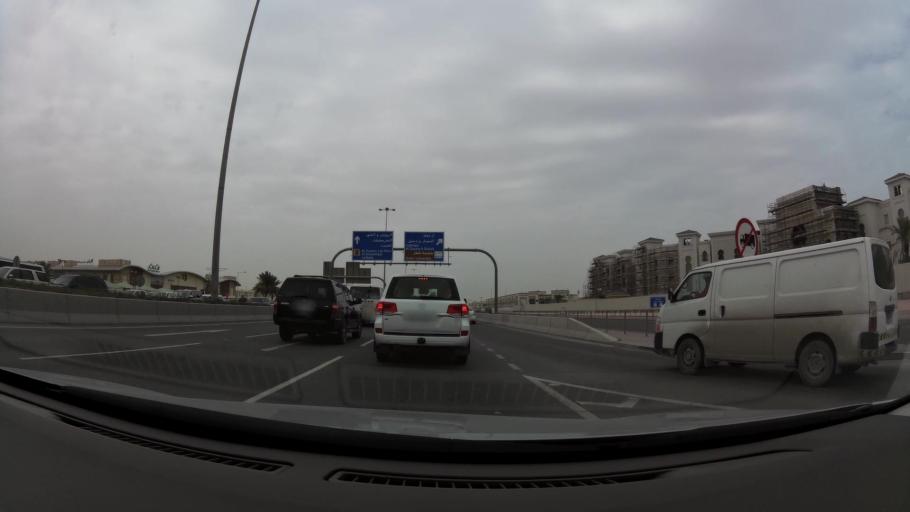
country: QA
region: Baladiyat ar Rayyan
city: Ar Rayyan
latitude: 25.3372
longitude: 51.4618
